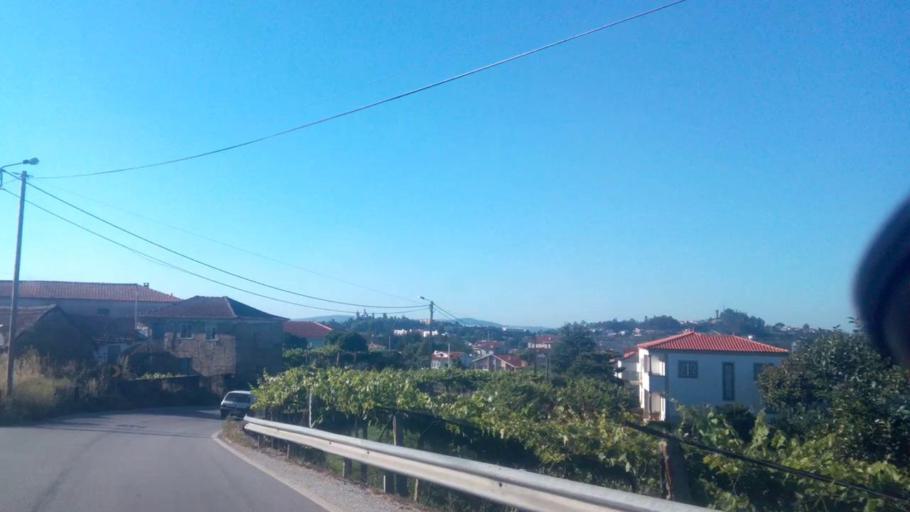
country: PT
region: Porto
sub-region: Penafiel
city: Penafiel
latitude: 41.1923
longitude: -8.2733
